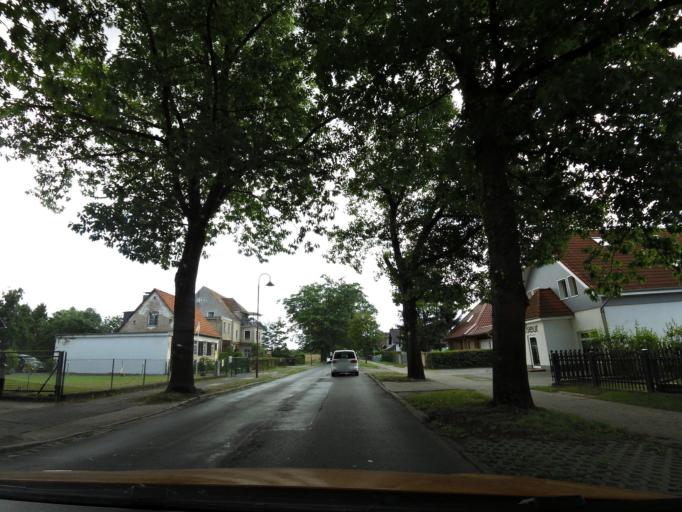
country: DE
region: Brandenburg
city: Rangsdorf
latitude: 52.3252
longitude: 13.4288
